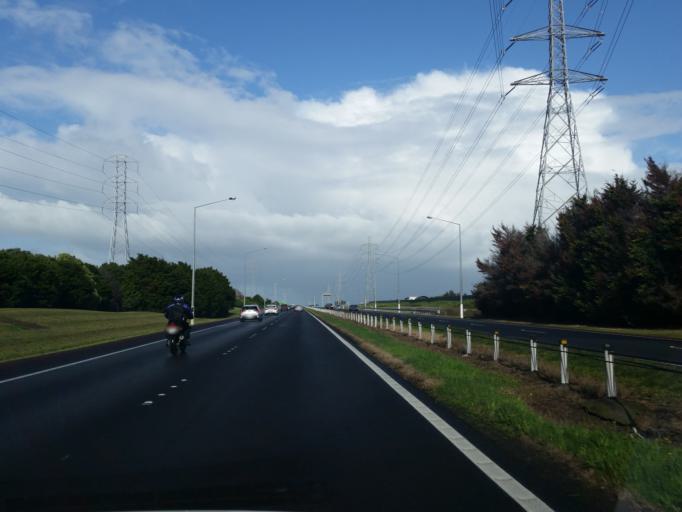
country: NZ
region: Auckland
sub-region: Auckland
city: Papakura
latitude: -37.0628
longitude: 174.9248
